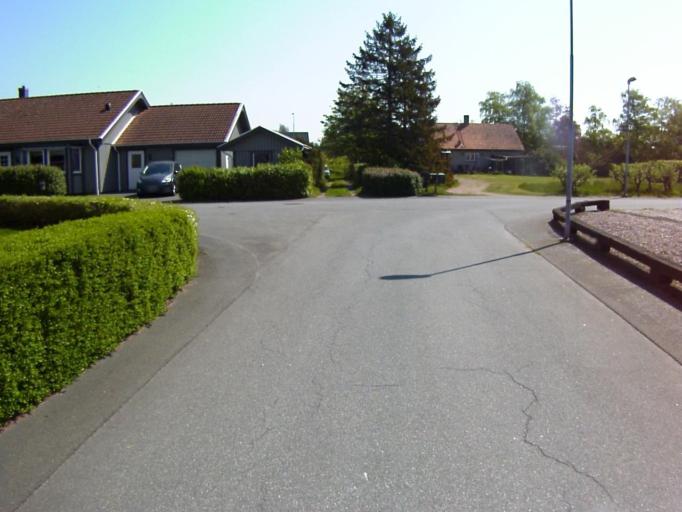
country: SE
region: Skane
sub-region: Kristianstads Kommun
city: Ahus
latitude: 55.9783
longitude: 14.2707
